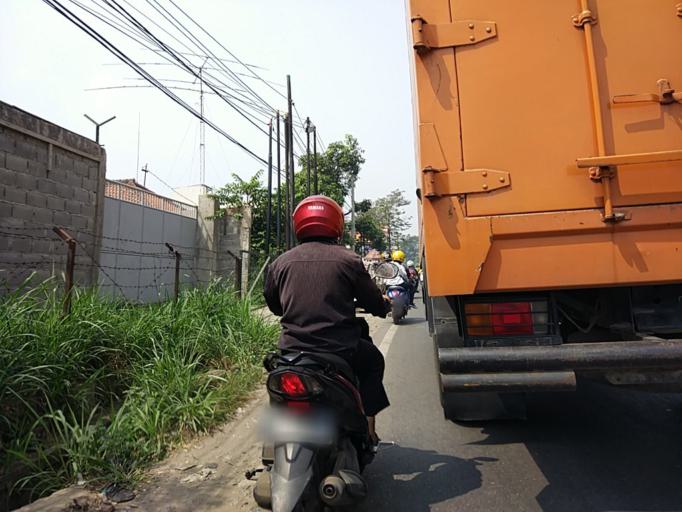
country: ID
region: West Java
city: Padalarang
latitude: -6.8596
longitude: 107.4993
